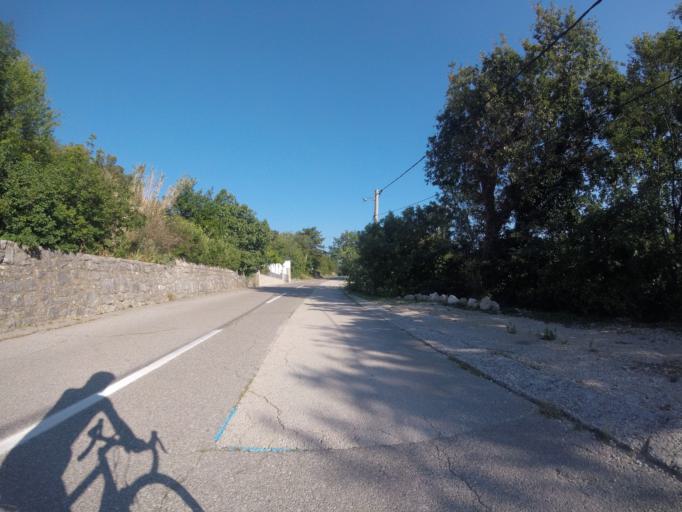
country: HR
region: Primorsko-Goranska
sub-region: Grad Crikvenica
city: Crikvenica
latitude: 45.2205
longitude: 14.6893
